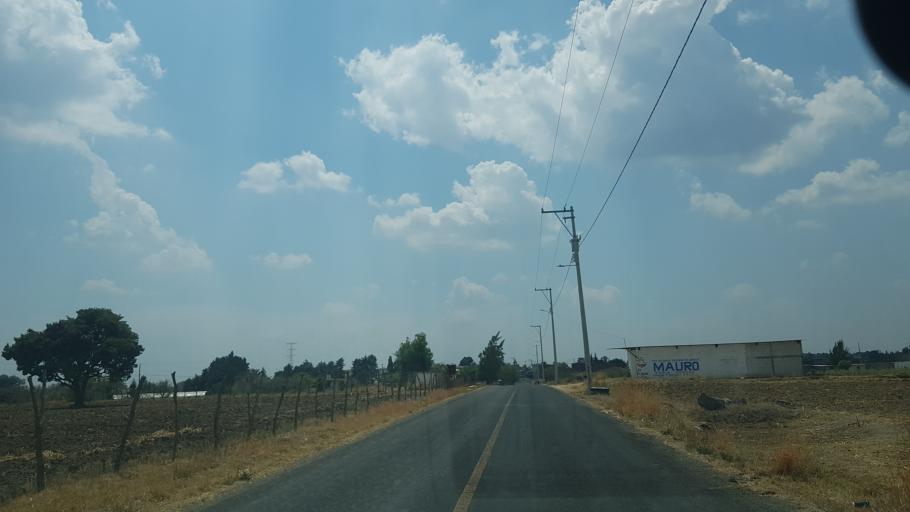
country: MX
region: Puebla
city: San Juan Amecac
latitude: 18.8281
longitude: -98.6515
